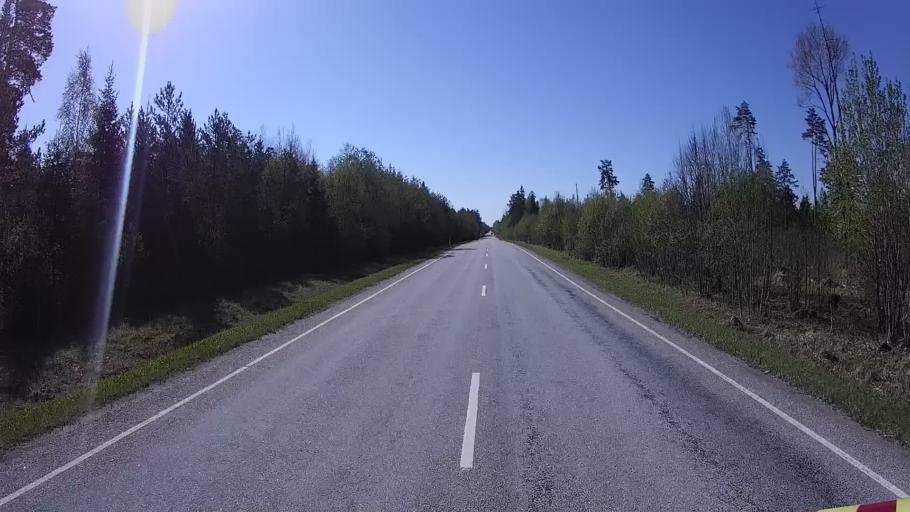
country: EE
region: Raplamaa
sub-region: Jaervakandi vald
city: Jarvakandi
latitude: 58.8143
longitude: 24.8050
